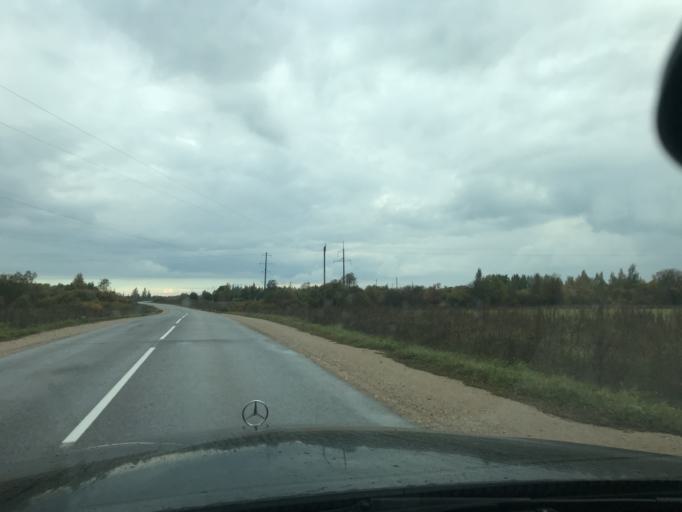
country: RU
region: Pskov
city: Izborsk
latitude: 57.6254
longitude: 27.9163
